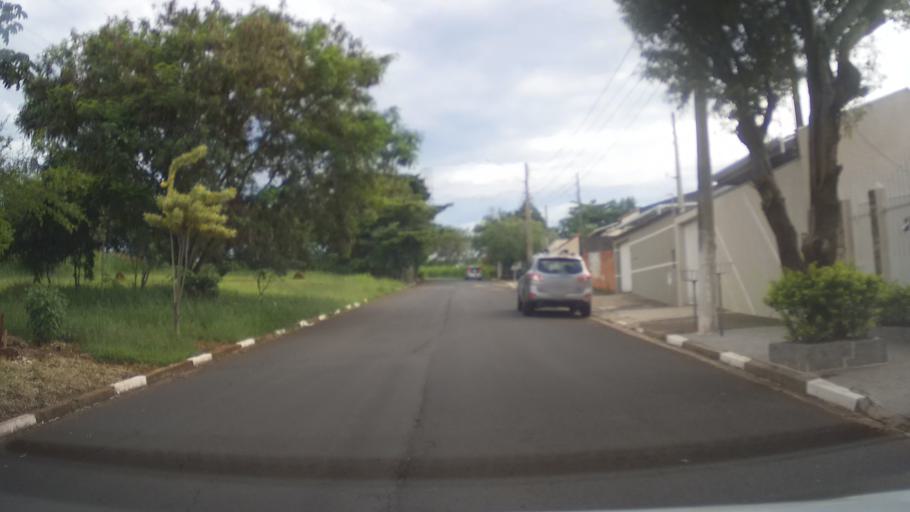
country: BR
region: Sao Paulo
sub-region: Campinas
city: Campinas
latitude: -22.8867
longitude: -47.1293
